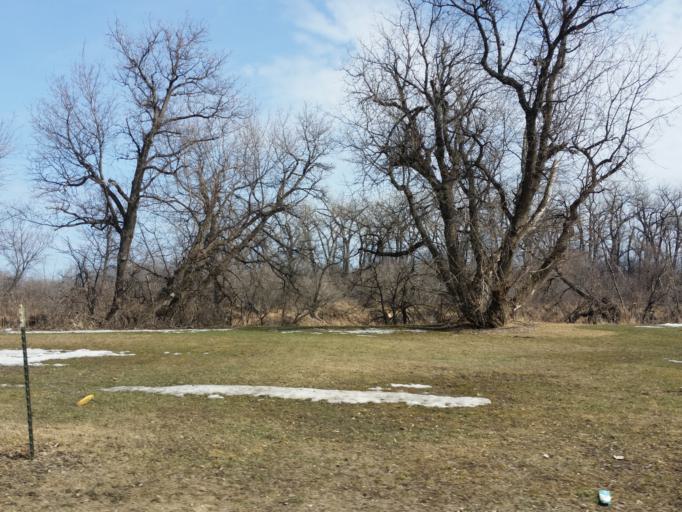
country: US
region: North Dakota
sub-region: Walsh County
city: Grafton
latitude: 48.4246
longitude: -97.4083
